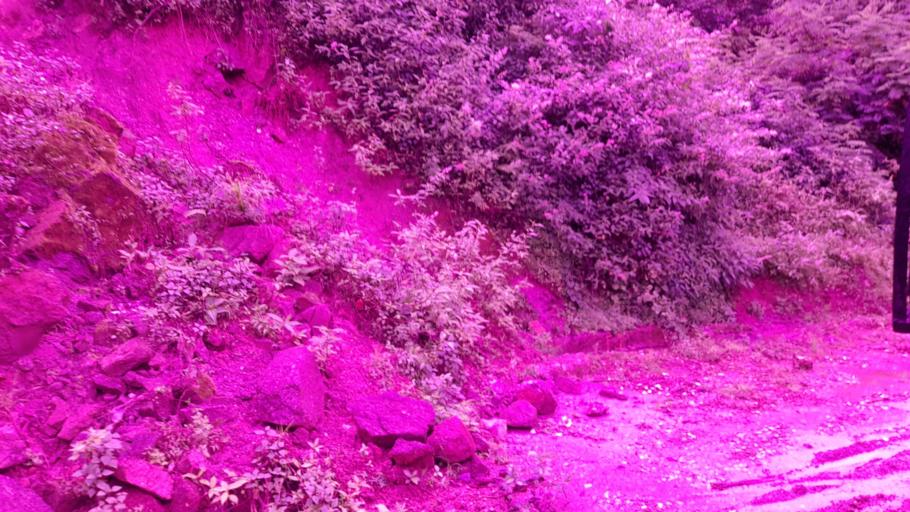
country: NP
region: Central Region
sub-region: Bagmati Zone
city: Kathmandu
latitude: 27.8186
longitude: 85.2440
